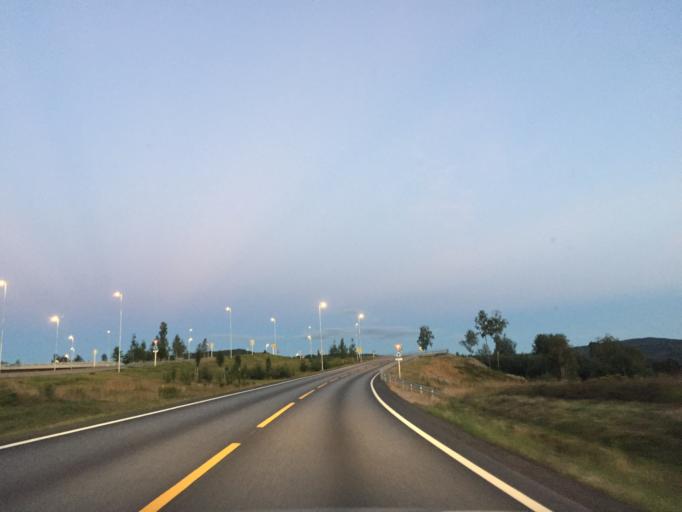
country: NO
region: Hedmark
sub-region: Kongsvinger
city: Spetalen
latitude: 60.2093
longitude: 11.8869
